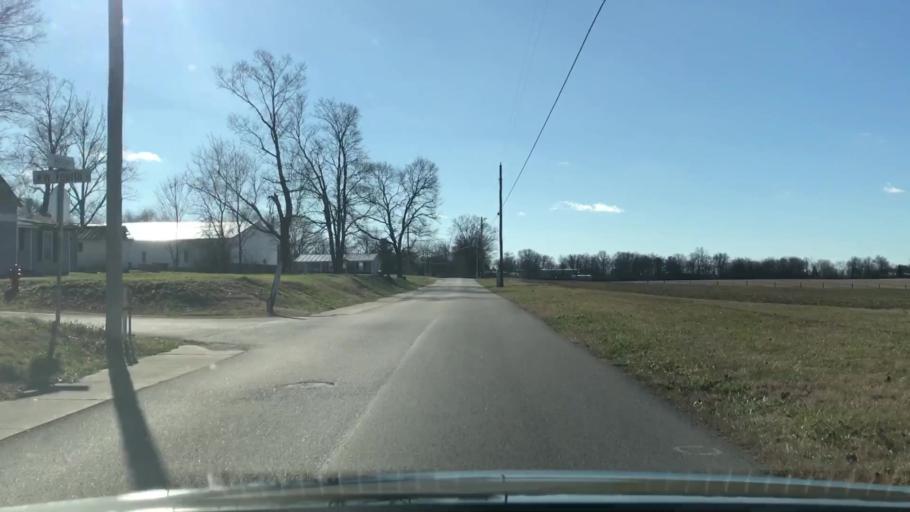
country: US
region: Kentucky
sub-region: Edmonson County
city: Brownsville
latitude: 37.0565
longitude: -86.2110
